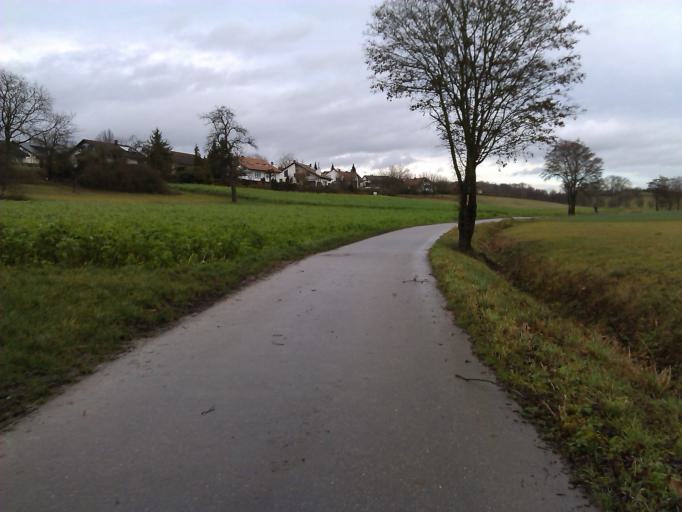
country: DE
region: Baden-Wuerttemberg
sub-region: Regierungsbezirk Stuttgart
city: Bad Wimpfen
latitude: 49.1959
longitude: 9.1529
